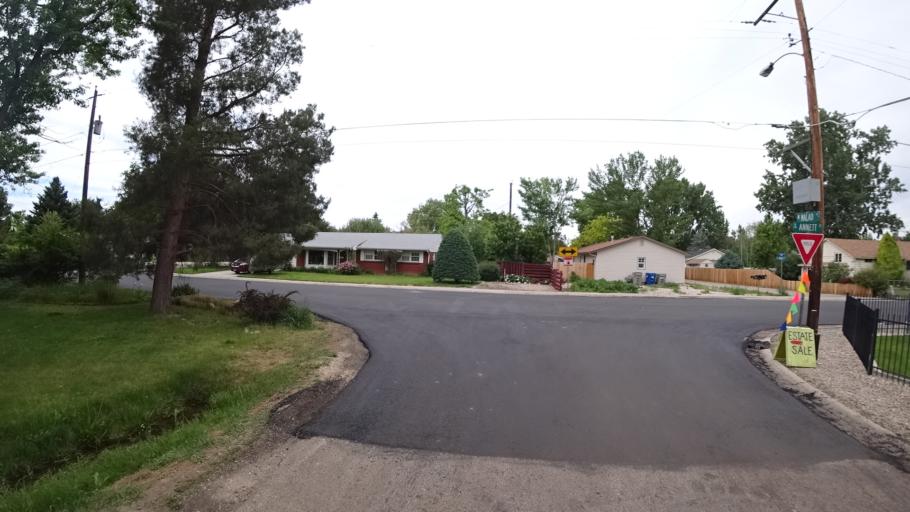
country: US
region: Idaho
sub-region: Ada County
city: Boise
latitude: 43.5790
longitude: -116.2035
